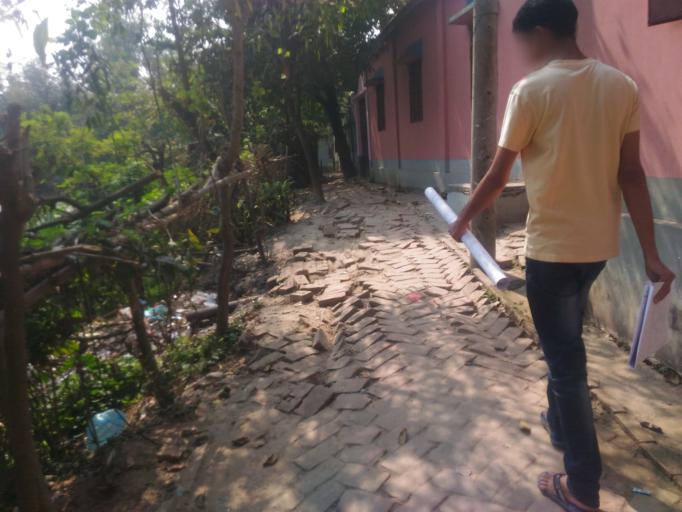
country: BD
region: Dhaka
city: Tungi
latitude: 24.0108
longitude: 90.3802
